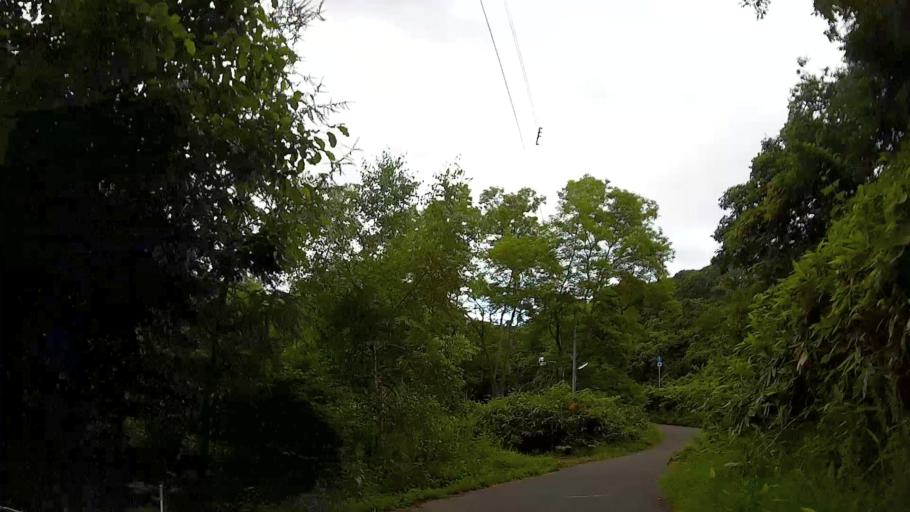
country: JP
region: Hokkaido
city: Nanae
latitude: 42.1179
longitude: 140.5361
